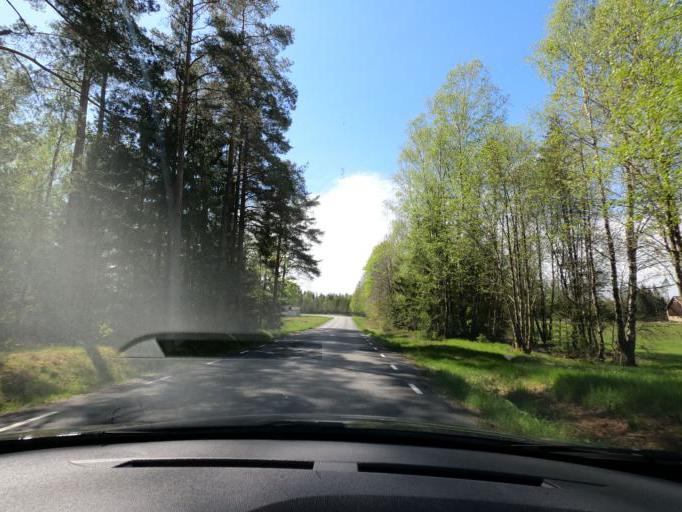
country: SE
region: Joenkoeping
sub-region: Varnamo Kommun
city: Bredaryd
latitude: 57.1543
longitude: 13.7339
